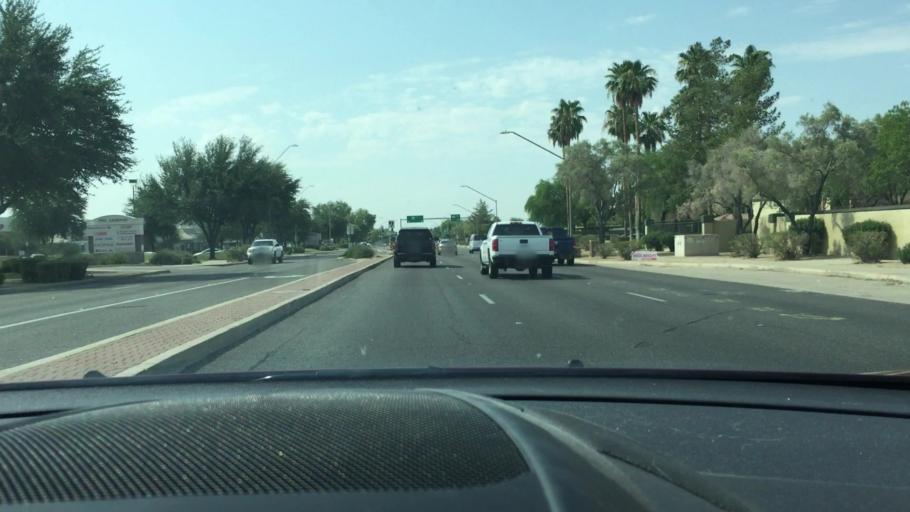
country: US
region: Arizona
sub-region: Maricopa County
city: Peoria
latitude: 33.6717
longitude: -112.2031
